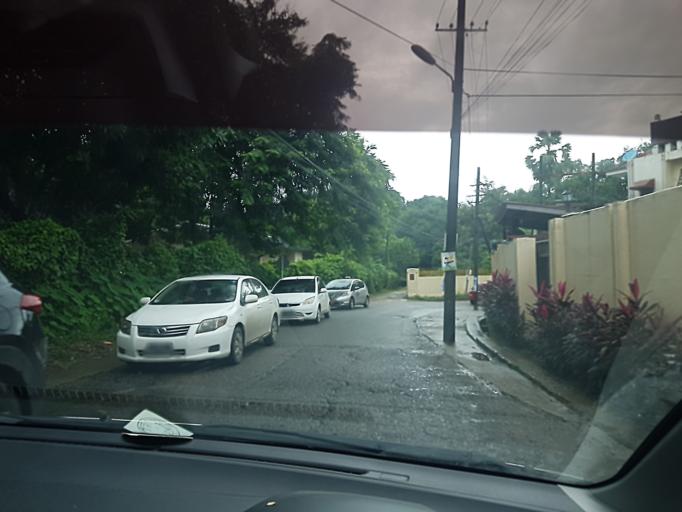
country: MM
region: Yangon
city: Yangon
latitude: 16.8116
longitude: 96.1427
